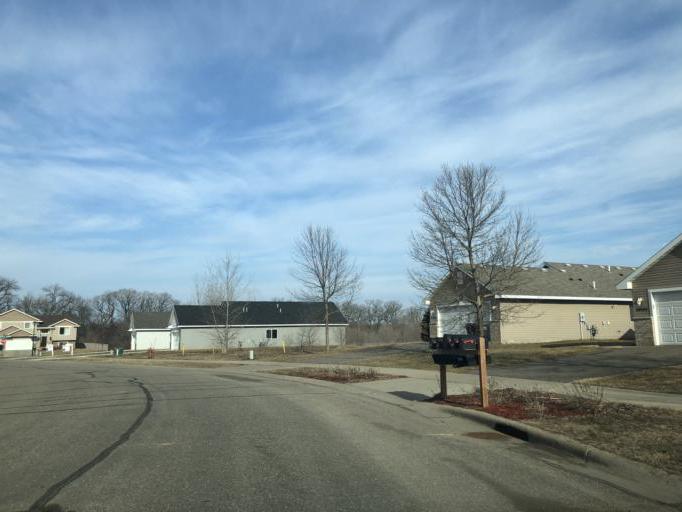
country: US
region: Minnesota
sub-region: Sherburne County
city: Becker
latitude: 45.4014
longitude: -93.8525
